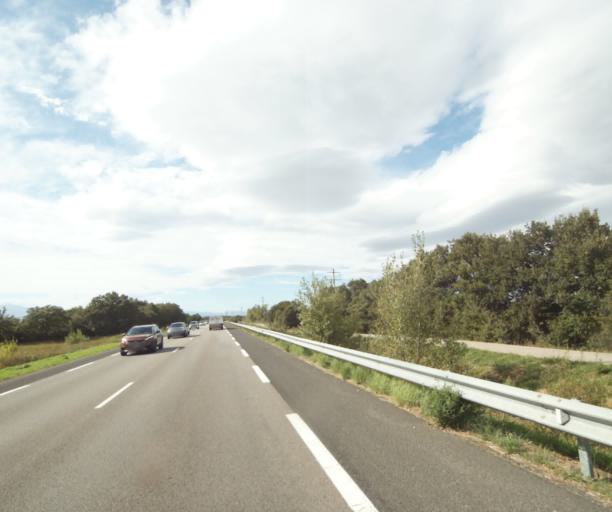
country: FR
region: Languedoc-Roussillon
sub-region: Departement des Pyrenees-Orientales
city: Sant Andreu de Sureda
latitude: 42.5560
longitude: 2.9831
